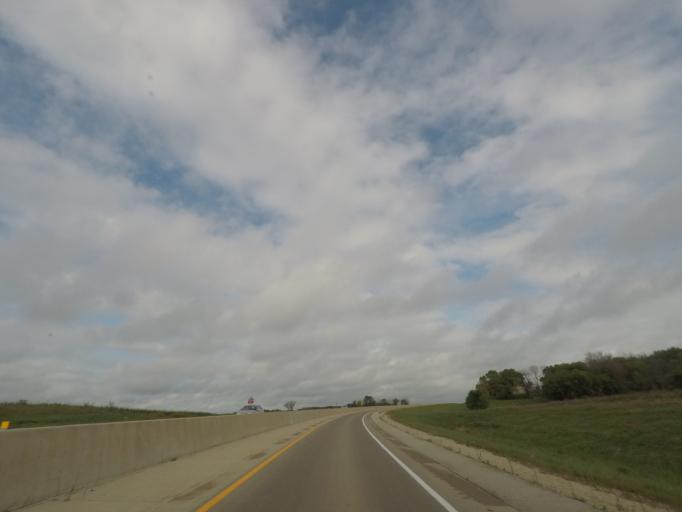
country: US
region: Wisconsin
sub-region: Dane County
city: Deerfield
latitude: 43.0216
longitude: -89.0692
